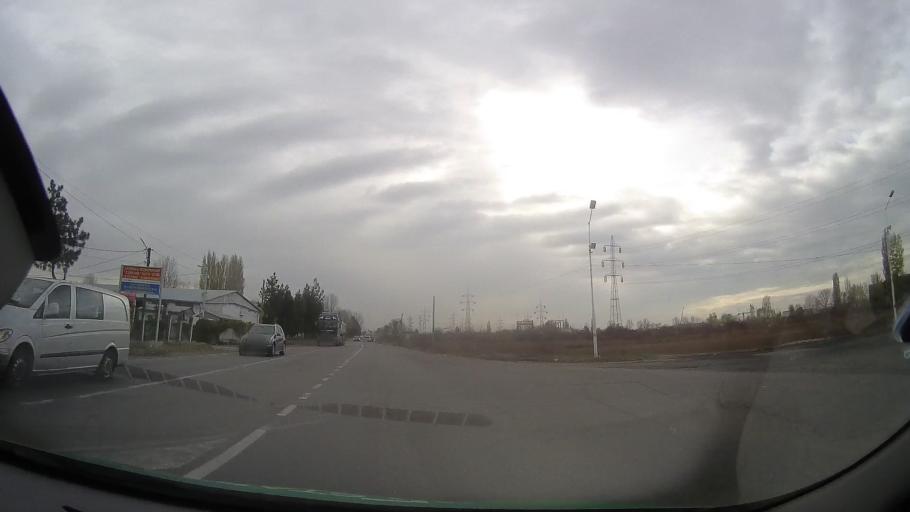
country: RO
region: Prahova
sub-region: Comuna Berceni
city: Berceni
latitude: 44.9459
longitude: 26.1001
